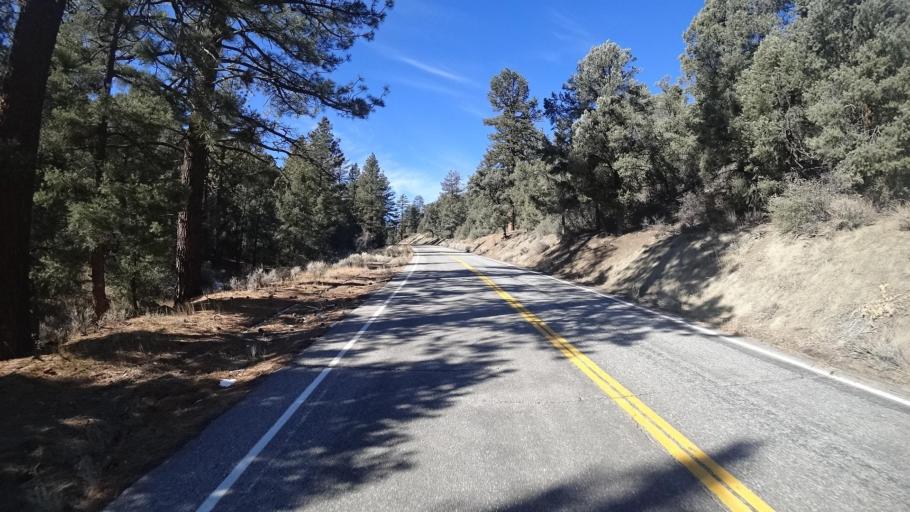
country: US
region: California
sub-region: Kern County
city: Pine Mountain Club
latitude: 34.8604
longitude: -119.2029
